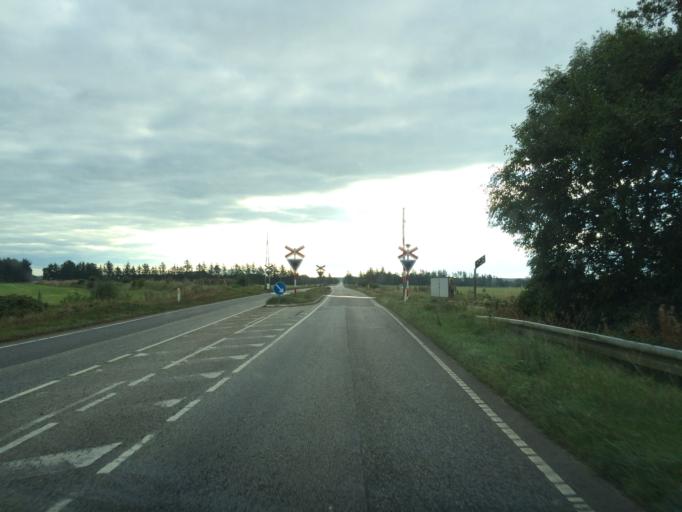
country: DK
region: Central Jutland
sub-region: Ringkobing-Skjern Kommune
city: Videbaek
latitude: 55.9631
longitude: 8.6672
